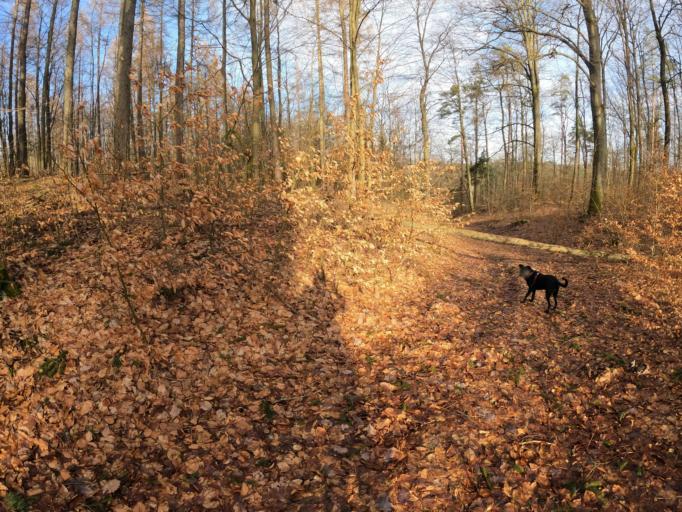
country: PL
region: West Pomeranian Voivodeship
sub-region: Powiat koszalinski
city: Polanow
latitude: 54.1242
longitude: 16.7003
